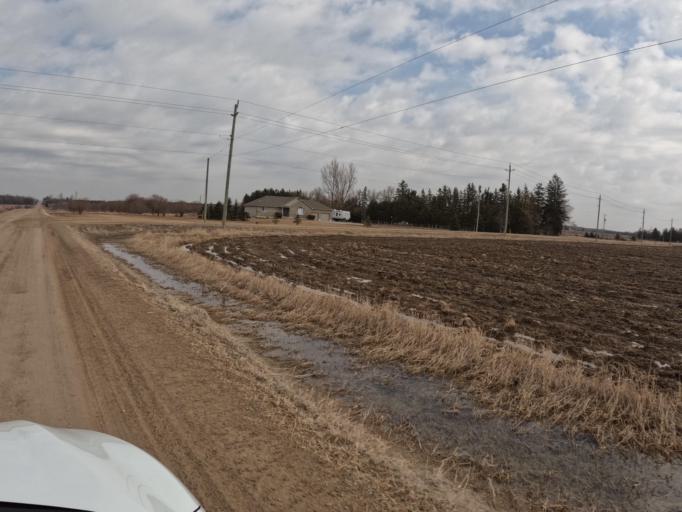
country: CA
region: Ontario
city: Orangeville
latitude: 43.9209
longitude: -80.2180
